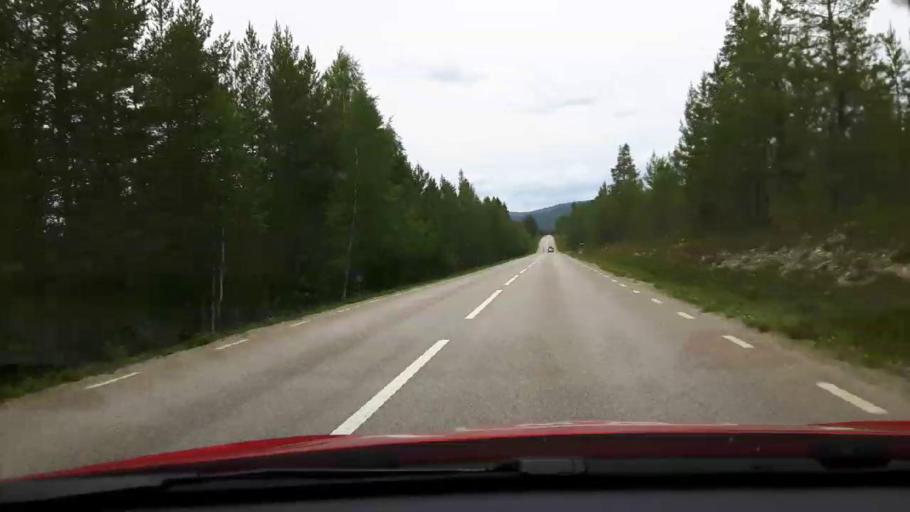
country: SE
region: Jaemtland
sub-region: Harjedalens Kommun
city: Sveg
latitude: 62.2473
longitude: 13.8432
